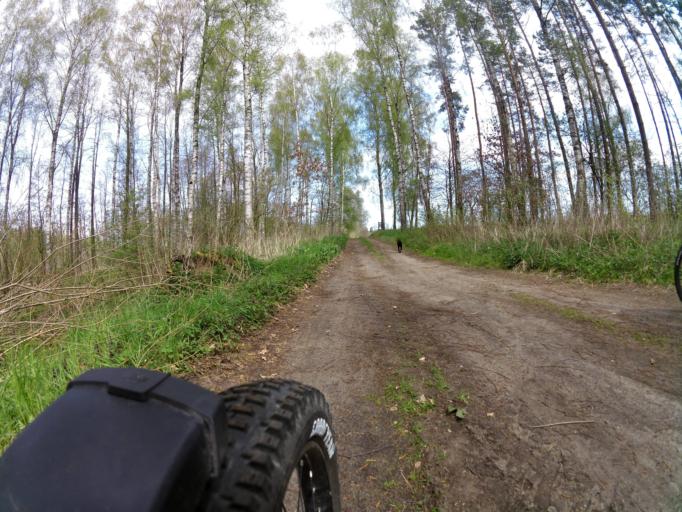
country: PL
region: West Pomeranian Voivodeship
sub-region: Powiat lobeski
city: Resko
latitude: 53.7634
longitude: 15.3801
